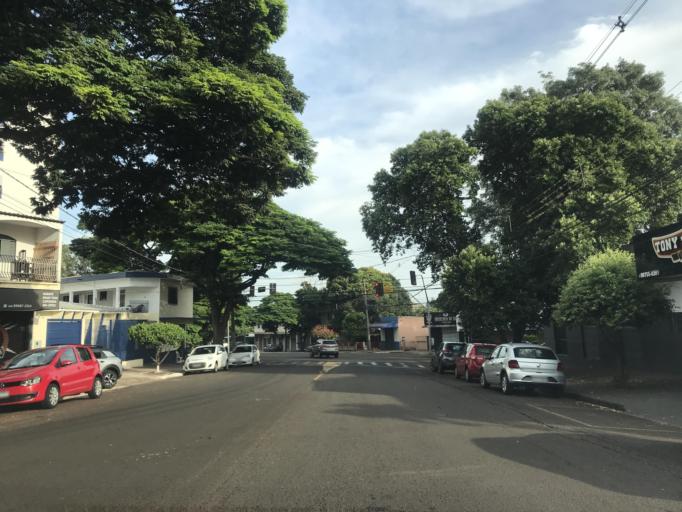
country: BR
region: Parana
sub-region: Maringa
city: Maringa
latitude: -23.4252
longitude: -51.9654
